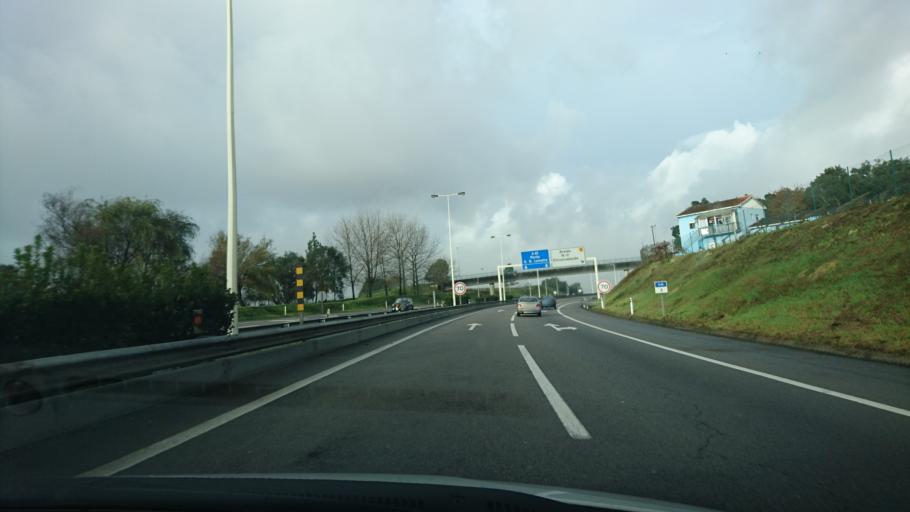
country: PT
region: Porto
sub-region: Gondomar
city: Valbom
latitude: 41.1557
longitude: -8.5571
